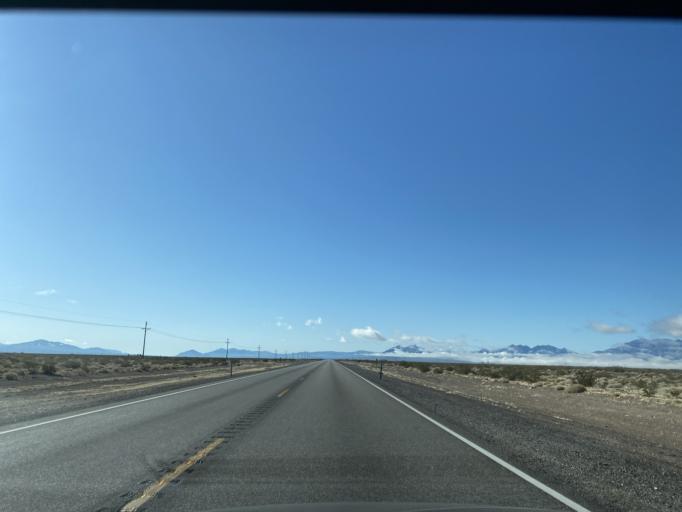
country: US
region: Nevada
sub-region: Nye County
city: Beatty
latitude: 36.5963
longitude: -116.4088
